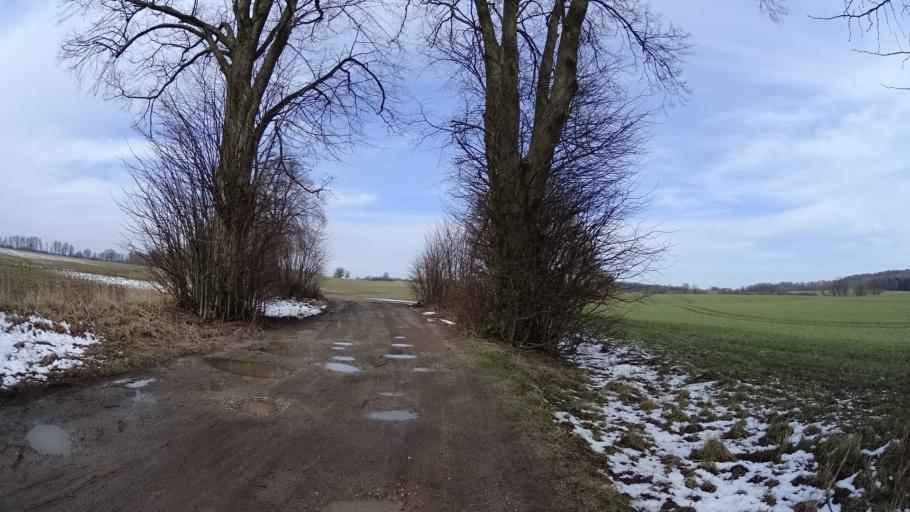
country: DE
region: Schleswig-Holstein
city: Loptin
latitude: 54.1603
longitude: 10.2329
